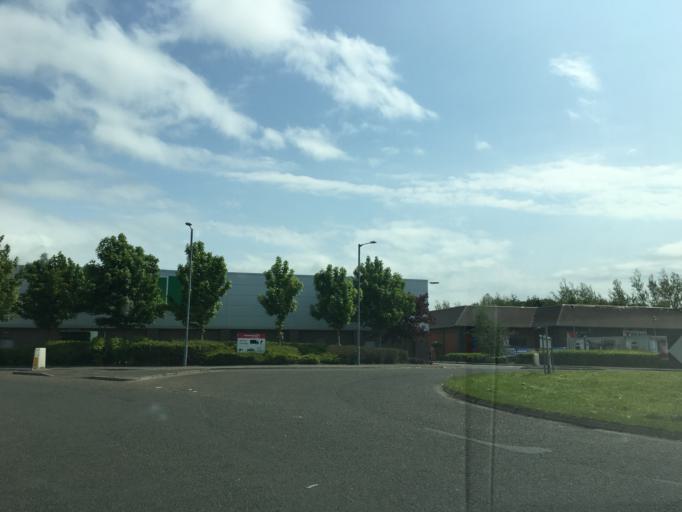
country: GB
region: Scotland
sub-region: Stirling
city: Bannockburn
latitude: 56.1125
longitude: -3.9099
